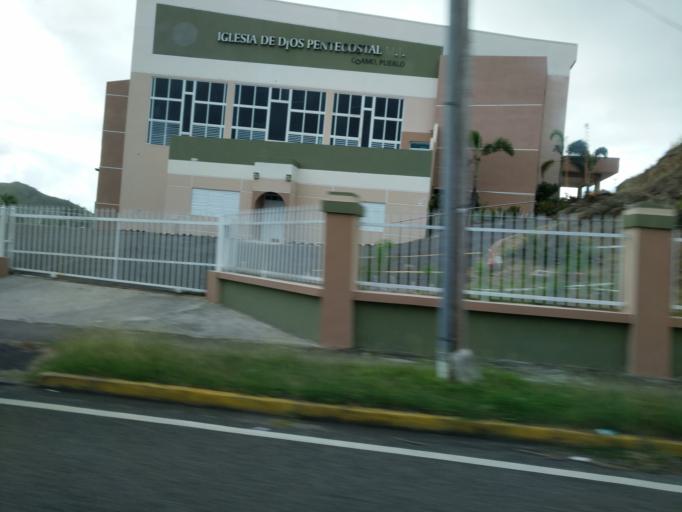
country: PR
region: Coamo
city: Coamo
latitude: 18.0769
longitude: -66.3679
